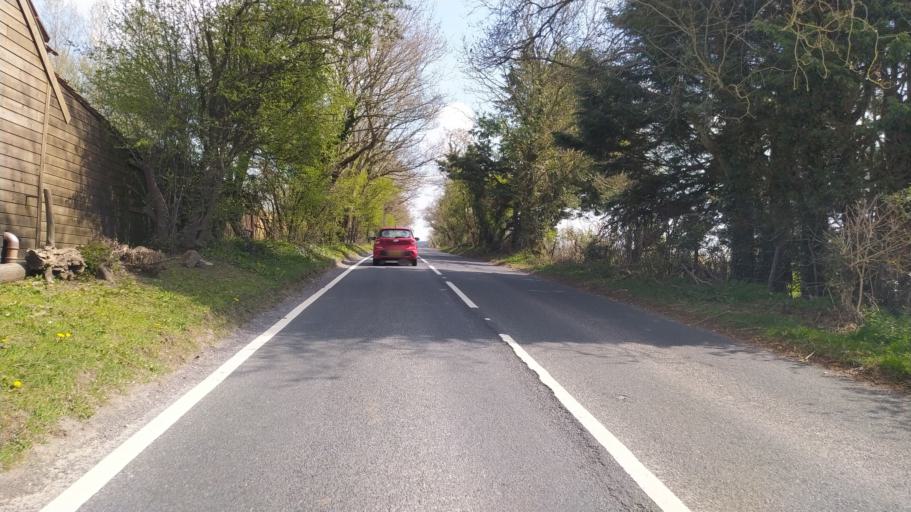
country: GB
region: England
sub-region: Wiltshire
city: Corsley
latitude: 51.2183
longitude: -2.2834
